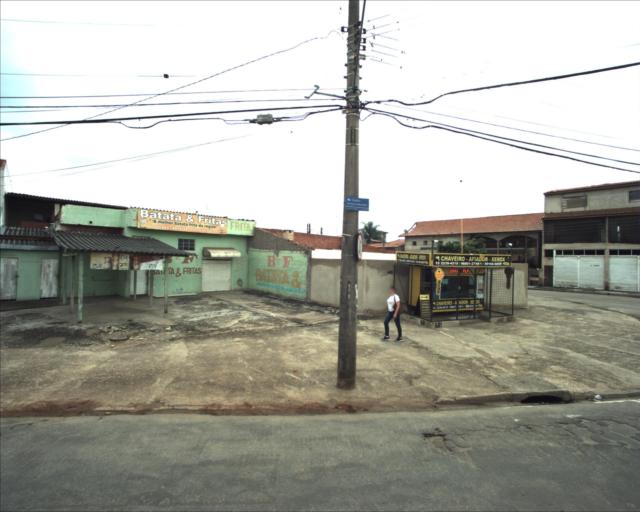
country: BR
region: Sao Paulo
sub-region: Sorocaba
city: Sorocaba
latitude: -23.4315
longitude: -47.4668
